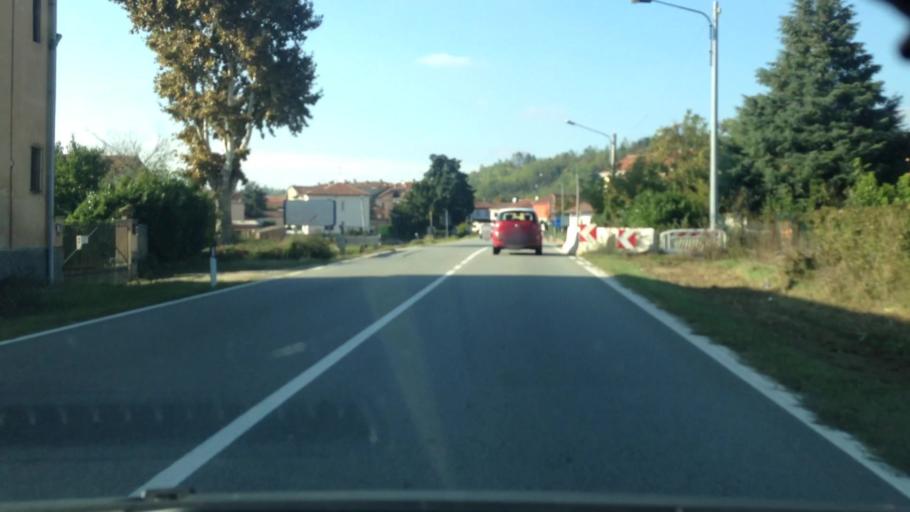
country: IT
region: Piedmont
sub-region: Provincia di Asti
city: Rocca d'Arazzo
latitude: 44.9056
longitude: 8.2858
